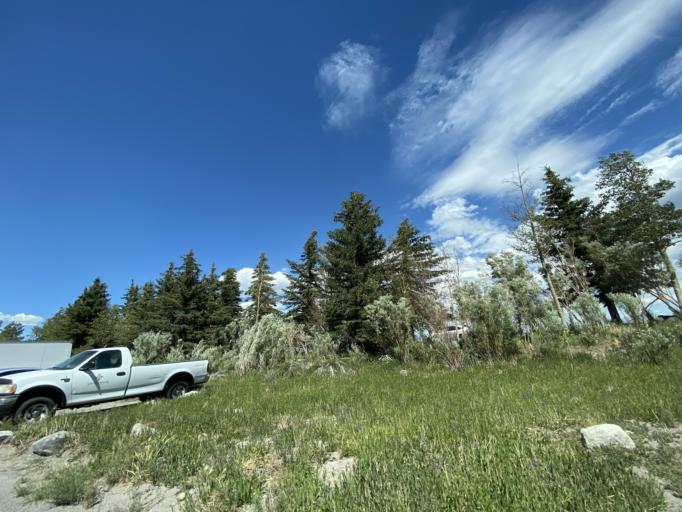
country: US
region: California
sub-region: Mono County
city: Mammoth Lakes
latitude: 37.6303
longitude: -118.9726
